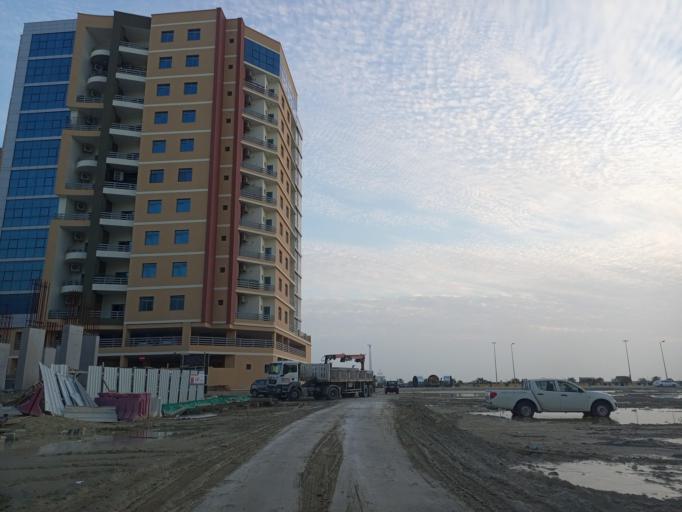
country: BH
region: Muharraq
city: Al Hadd
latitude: 26.2272
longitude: 50.6501
